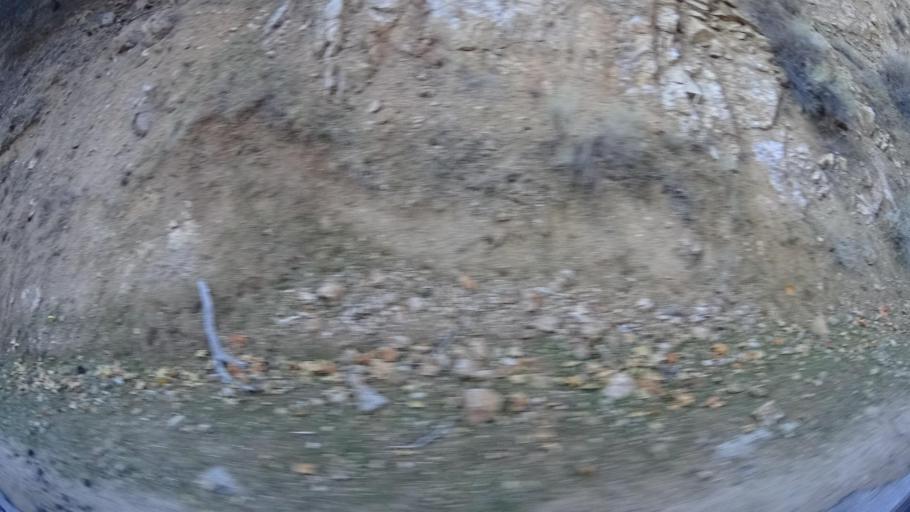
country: US
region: California
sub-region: Kern County
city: Golden Hills
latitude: 35.3016
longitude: -118.4729
